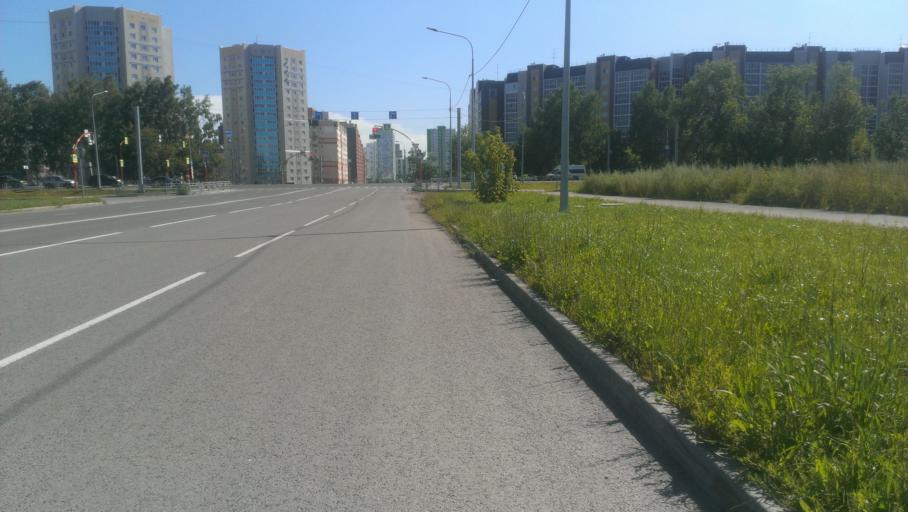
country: RU
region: Altai Krai
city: Novosilikatnyy
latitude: 53.3476
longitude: 83.6501
